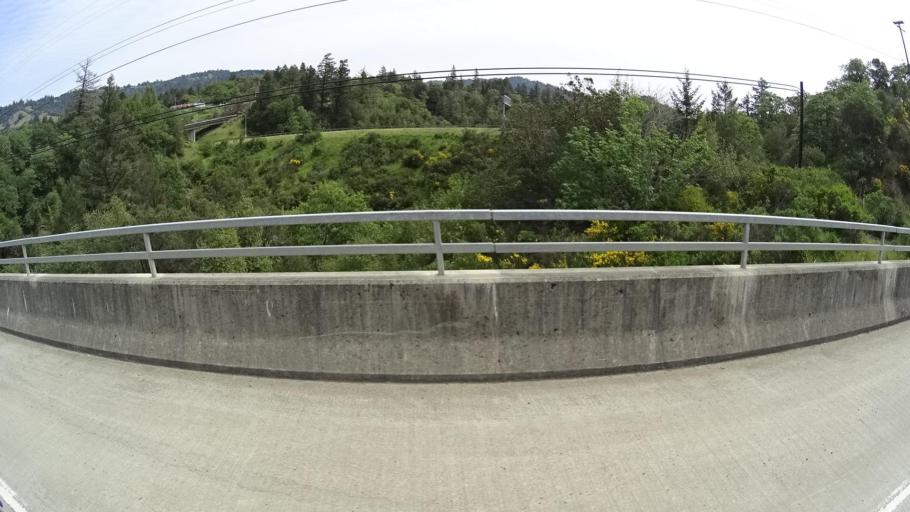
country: US
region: California
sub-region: Humboldt County
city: Redway
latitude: 40.1068
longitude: -123.7962
